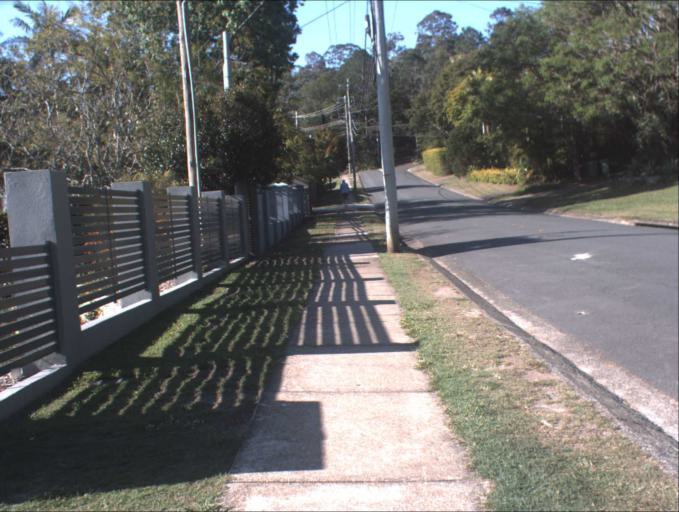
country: AU
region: Queensland
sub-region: Logan
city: Slacks Creek
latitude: -27.6263
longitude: 153.1553
